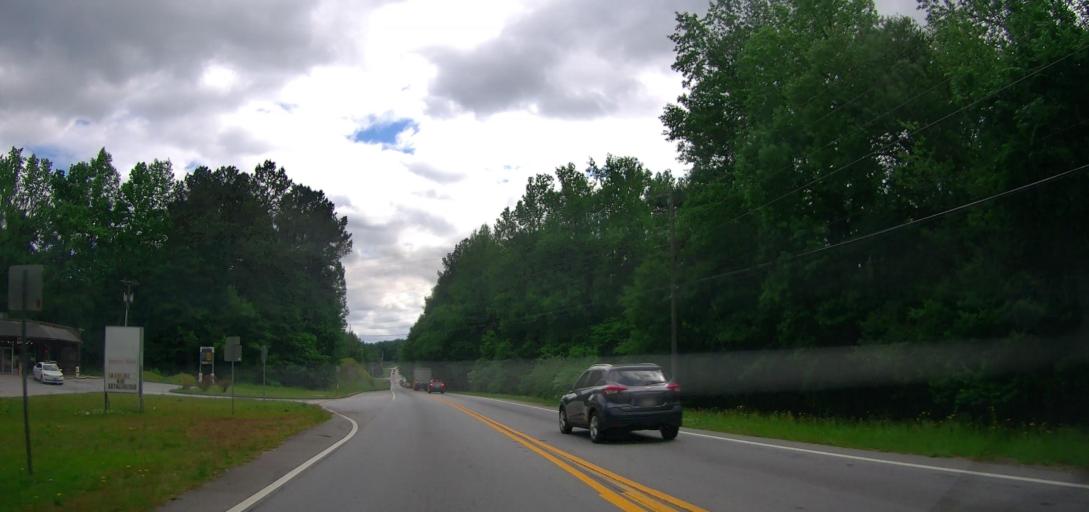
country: US
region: Georgia
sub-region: Walton County
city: Walnut Grove
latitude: 33.7145
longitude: -83.9296
